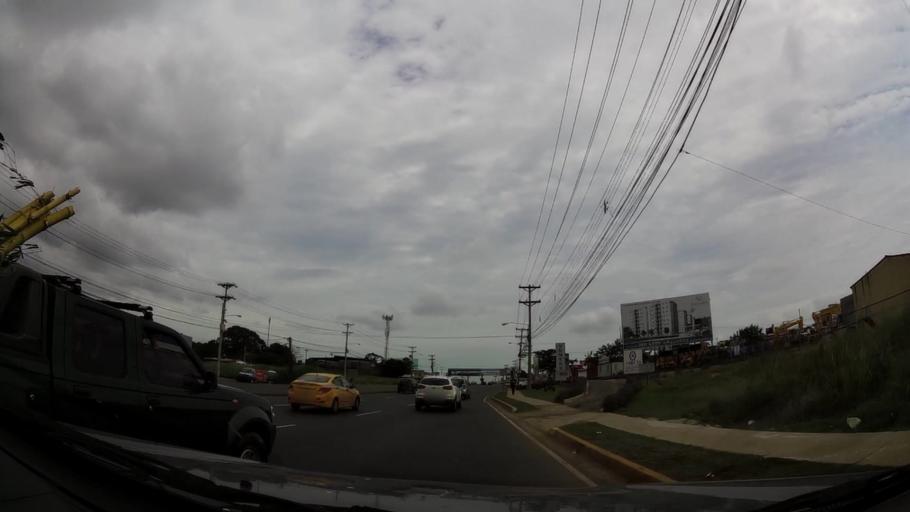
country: PA
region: Panama
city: San Miguelito
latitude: 9.0611
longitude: -79.4249
